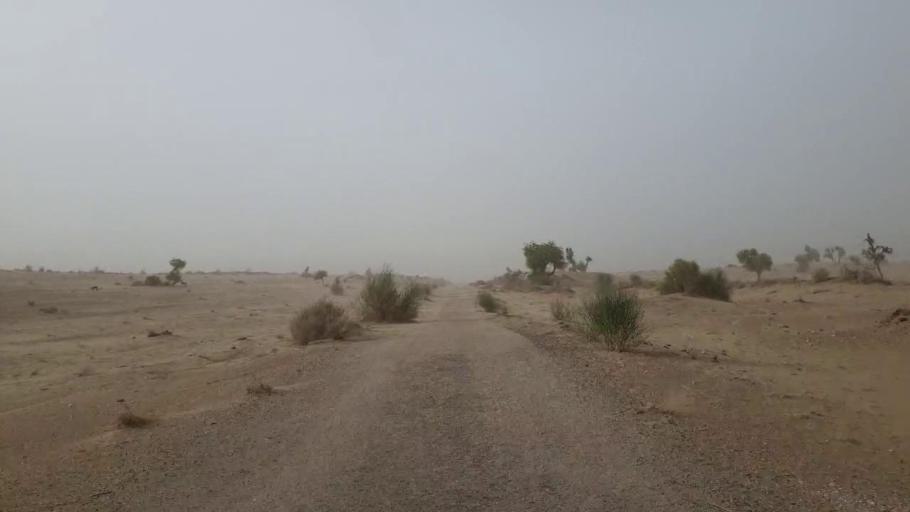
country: PK
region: Sindh
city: Islamkot
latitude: 24.5645
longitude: 70.3627
